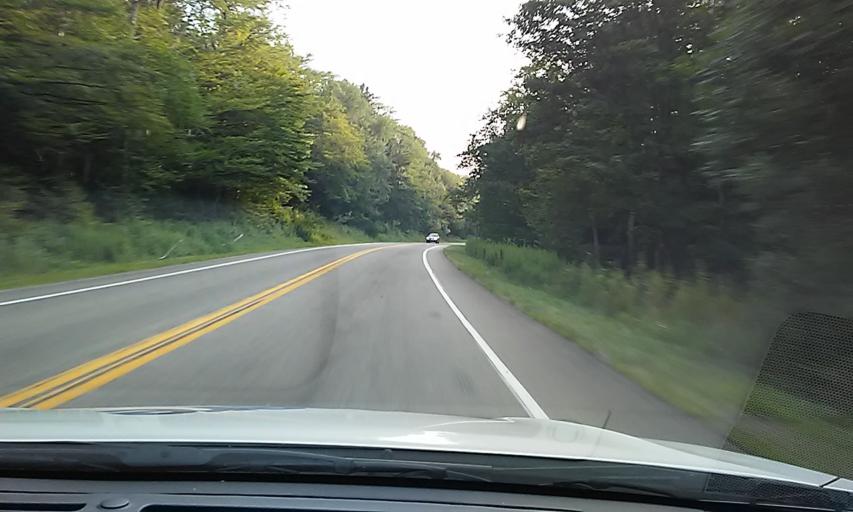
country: US
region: Pennsylvania
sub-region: Forest County
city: Marienville
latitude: 41.5521
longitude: -79.0119
